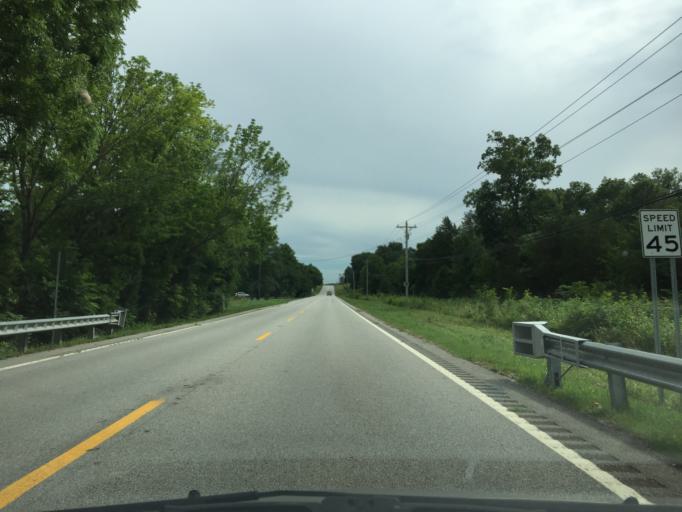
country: US
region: Tennessee
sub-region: Bradley County
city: Hopewell
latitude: 35.2928
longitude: -84.9664
